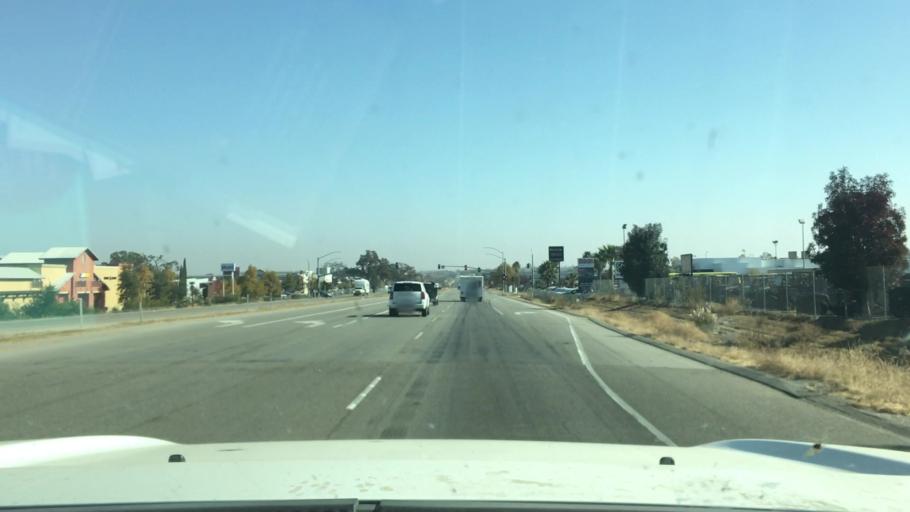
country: US
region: California
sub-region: San Luis Obispo County
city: Paso Robles
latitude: 35.6445
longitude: -120.6605
